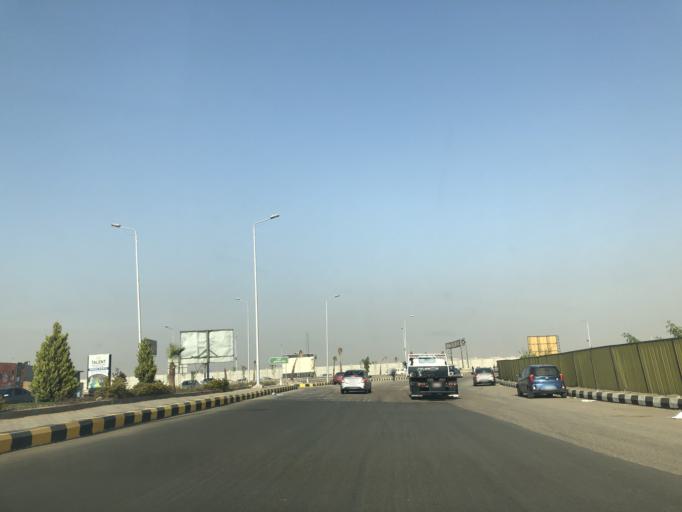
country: EG
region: Al Jizah
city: Madinat Sittah Uktubar
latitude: 29.9550
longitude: 31.0768
